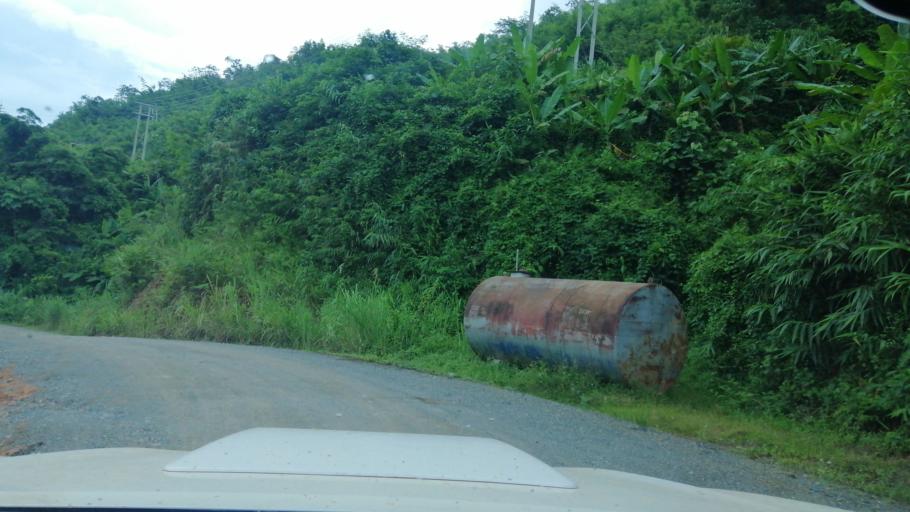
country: LA
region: Xiagnabouli
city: Sainyabuli
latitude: 19.1843
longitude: 101.7985
